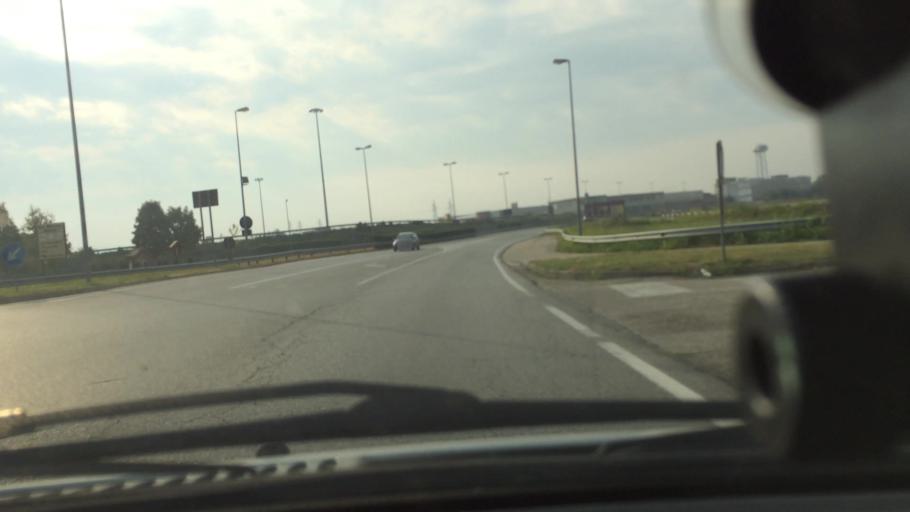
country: IT
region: Piedmont
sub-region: Provincia di Torino
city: Villastellone
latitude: 44.9168
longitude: 7.7417
